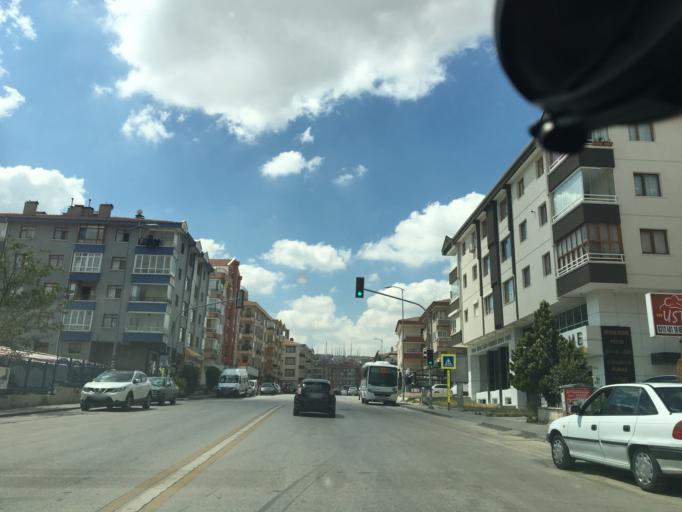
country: TR
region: Ankara
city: Ankara
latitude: 39.8880
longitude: 32.8289
